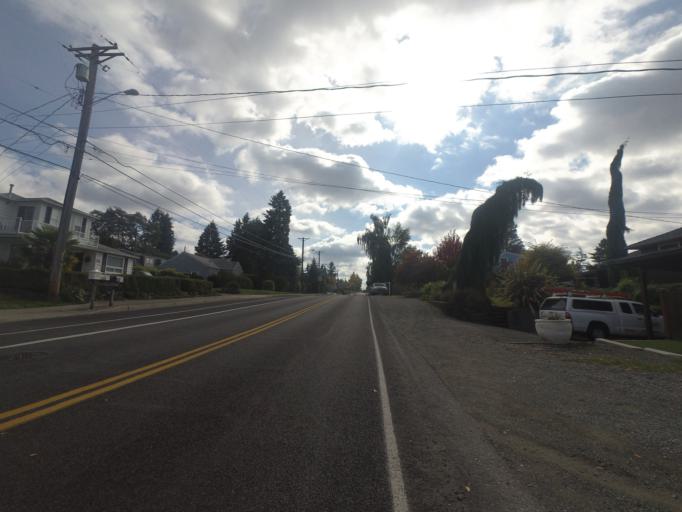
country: US
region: Washington
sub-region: Pierce County
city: University Place
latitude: 47.2323
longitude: -122.5453
